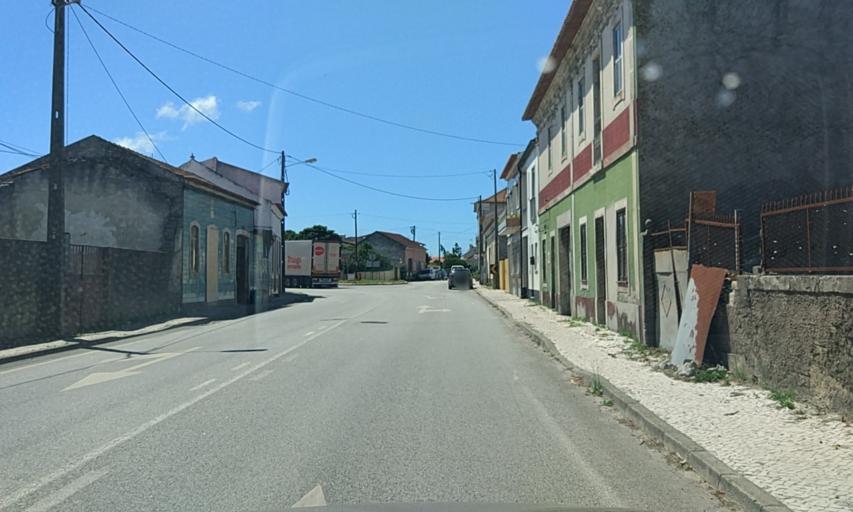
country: PT
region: Coimbra
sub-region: Mira
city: Mira
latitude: 40.4239
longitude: -8.7371
